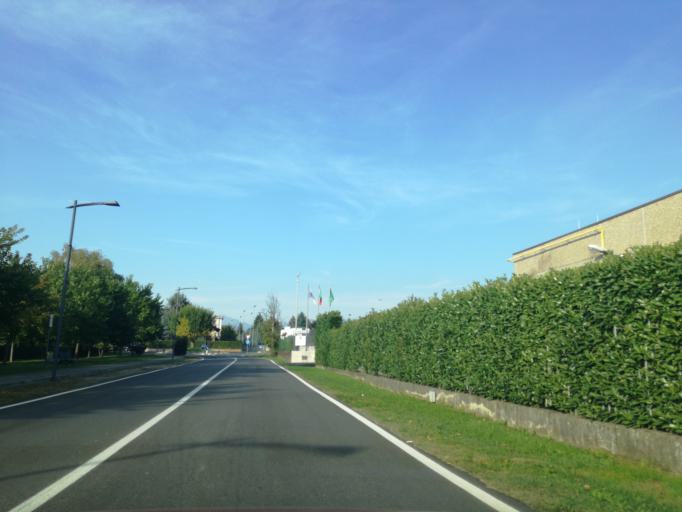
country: IT
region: Lombardy
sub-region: Provincia di Monza e Brianza
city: Aicurzio
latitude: 45.6376
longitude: 9.4183
